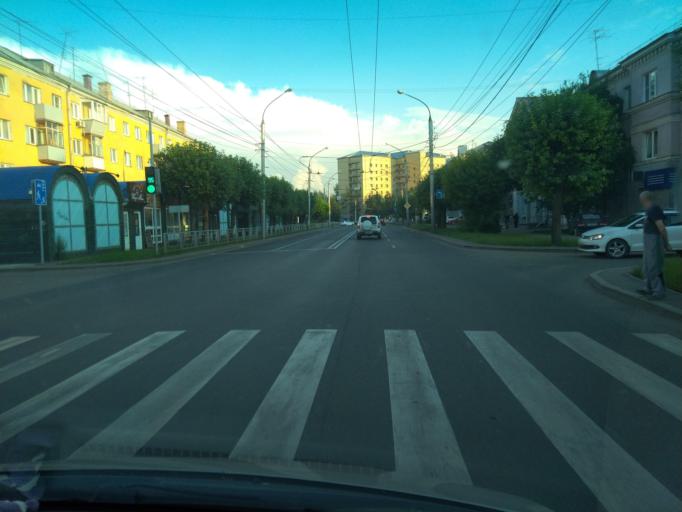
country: RU
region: Krasnoyarskiy
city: Krasnoyarsk
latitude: 56.0279
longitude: 92.9074
